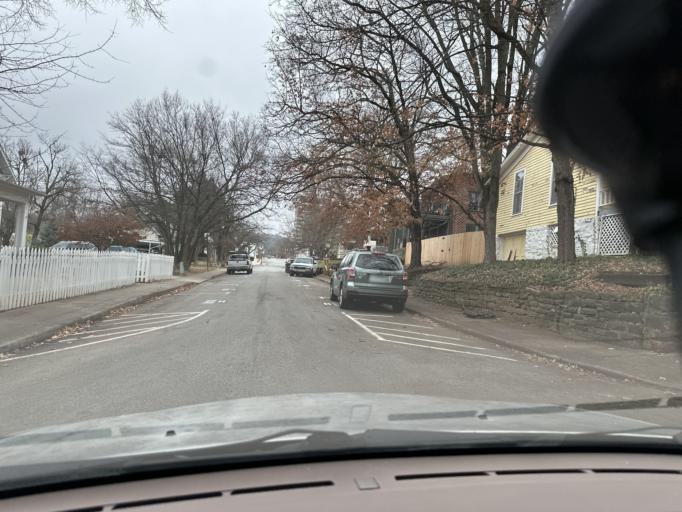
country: US
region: Arkansas
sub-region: Washington County
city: Fayetteville
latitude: 36.0637
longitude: -94.1631
